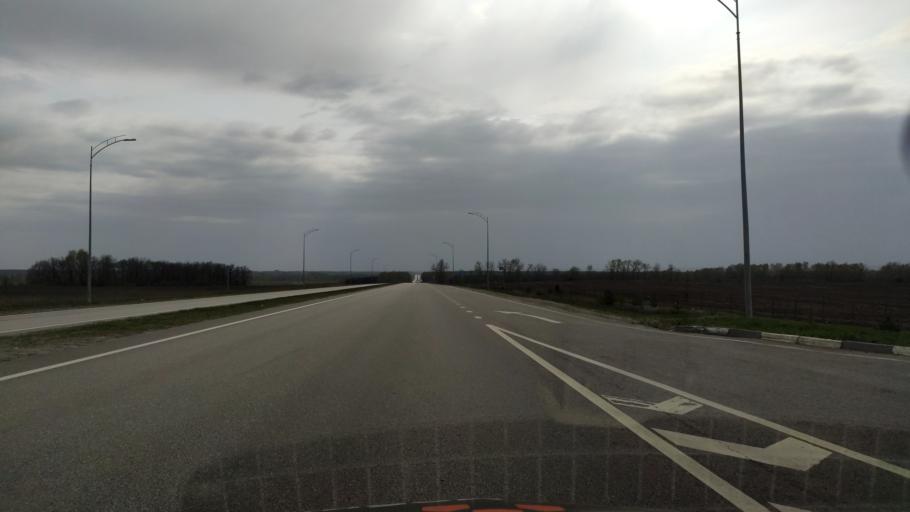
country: RU
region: Belgorod
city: Staryy Oskol
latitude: 51.4205
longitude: 37.8911
